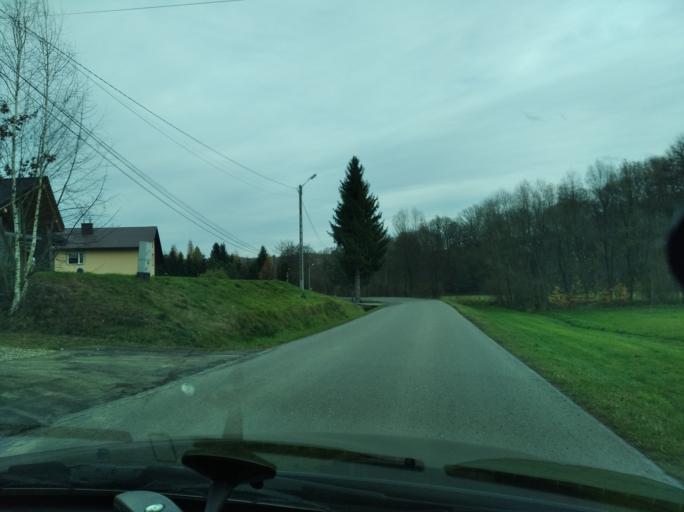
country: PL
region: Subcarpathian Voivodeship
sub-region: Powiat ropczycko-sedziszowski
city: Iwierzyce
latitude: 49.9465
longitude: 21.7377
